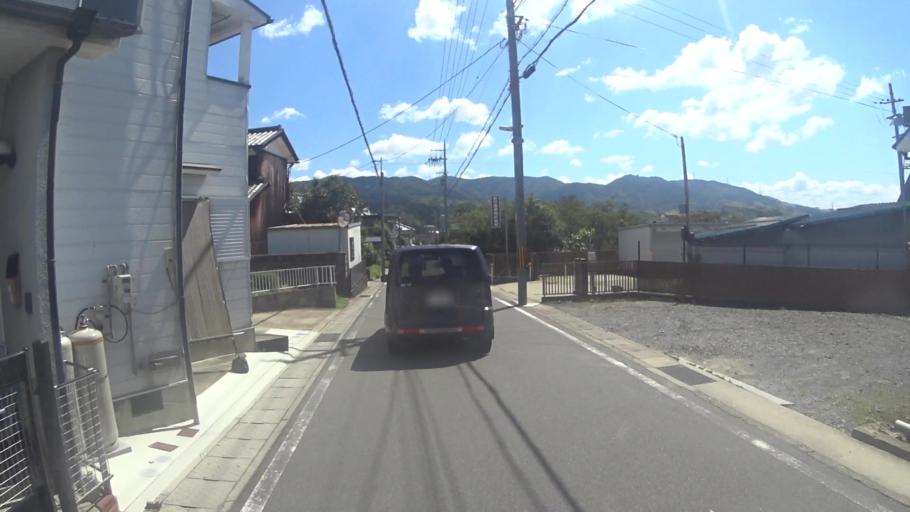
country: JP
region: Kyoto
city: Tanabe
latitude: 34.8327
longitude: 135.8006
